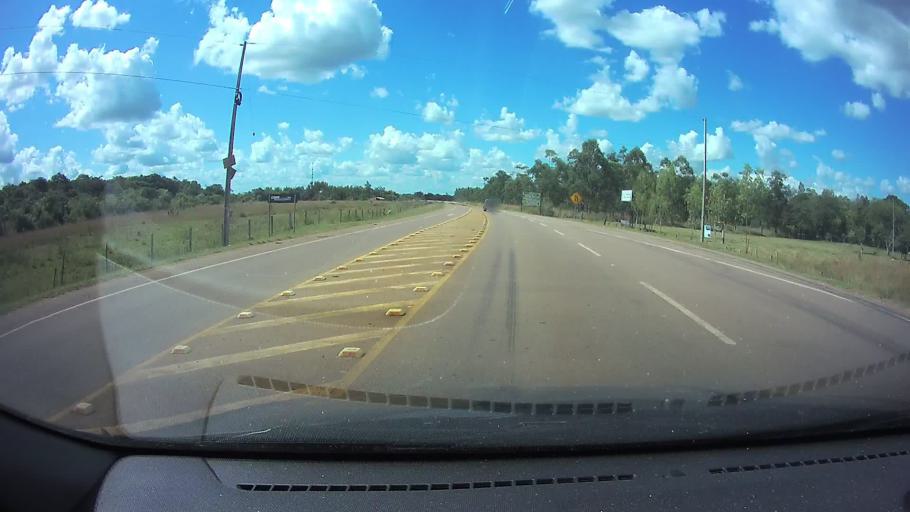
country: PY
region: Guaira
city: Itape
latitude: -25.9088
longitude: -56.6751
